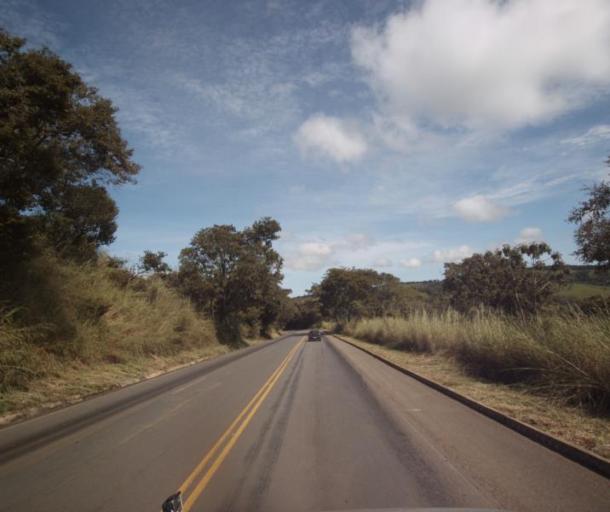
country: BR
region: Goias
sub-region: Abadiania
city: Abadiania
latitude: -16.1028
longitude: -48.8619
